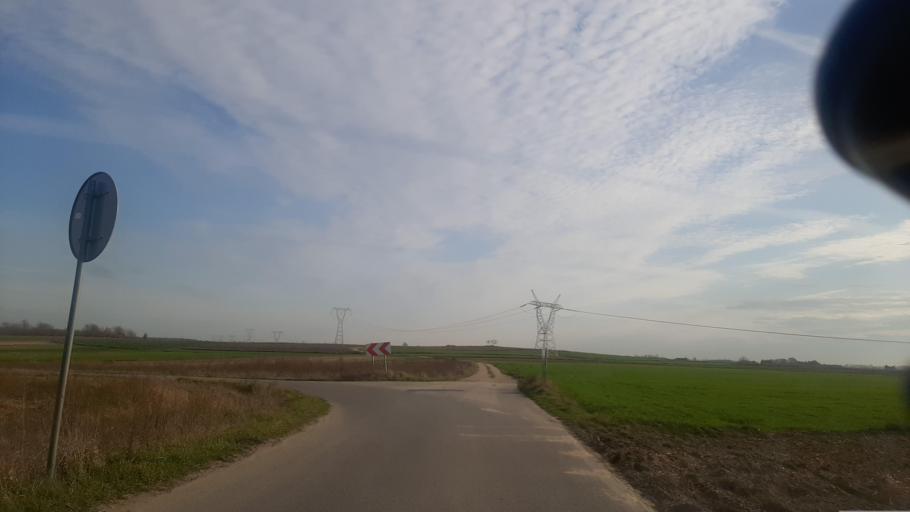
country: PL
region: Lublin Voivodeship
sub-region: Powiat lubelski
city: Garbow
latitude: 51.3827
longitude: 22.3451
